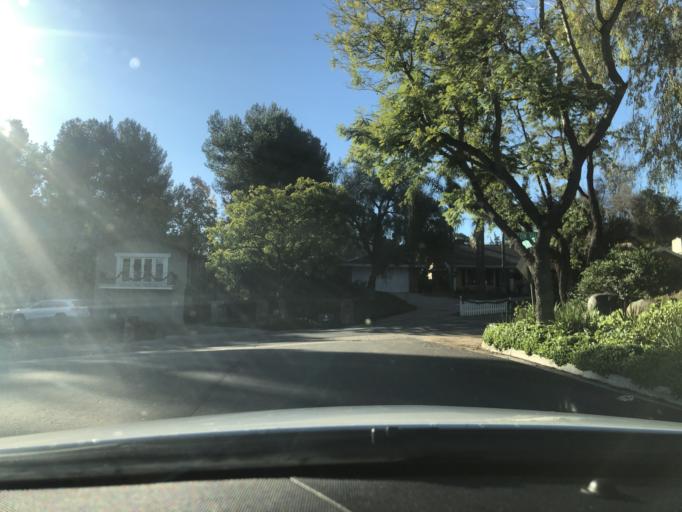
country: US
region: California
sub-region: San Diego County
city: Casa de Oro-Mount Helix
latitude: 32.7705
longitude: -116.9587
